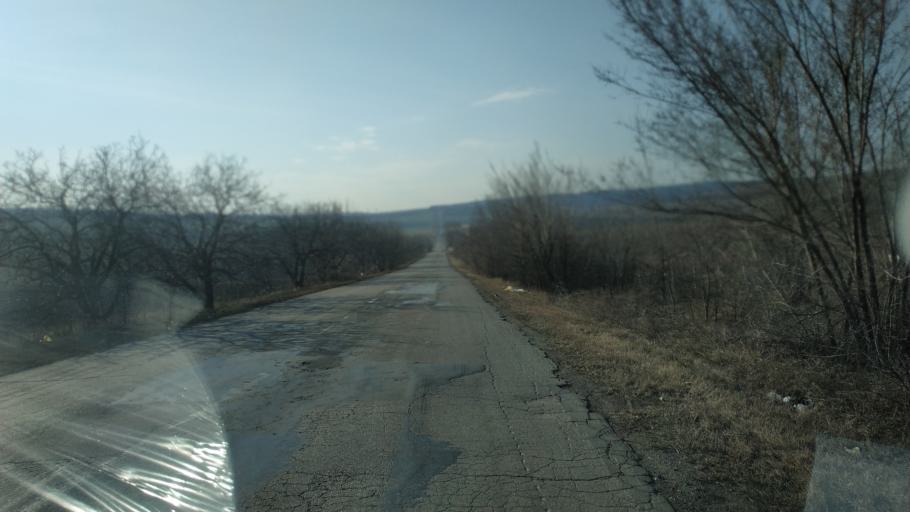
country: MD
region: Chisinau
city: Singera
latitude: 46.8916
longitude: 29.0390
